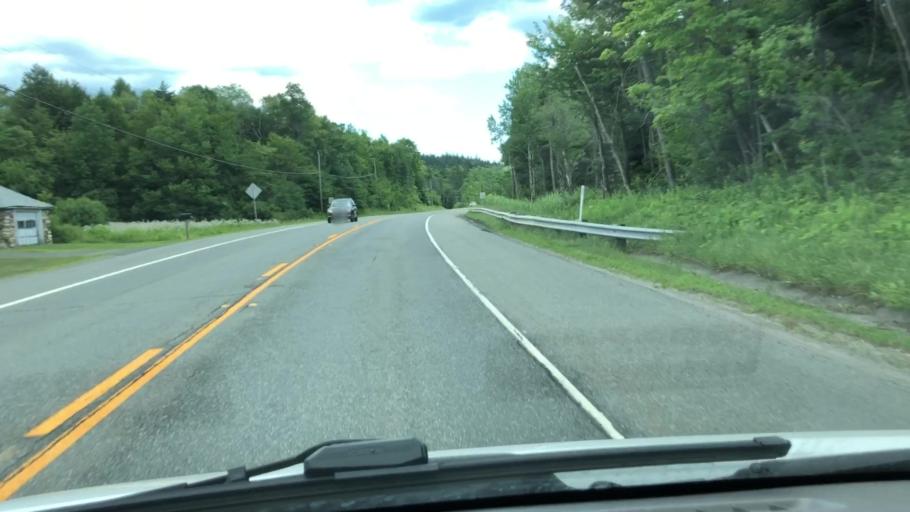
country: US
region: Massachusetts
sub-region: Berkshire County
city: Hinsdale
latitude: 42.5088
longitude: -73.0453
